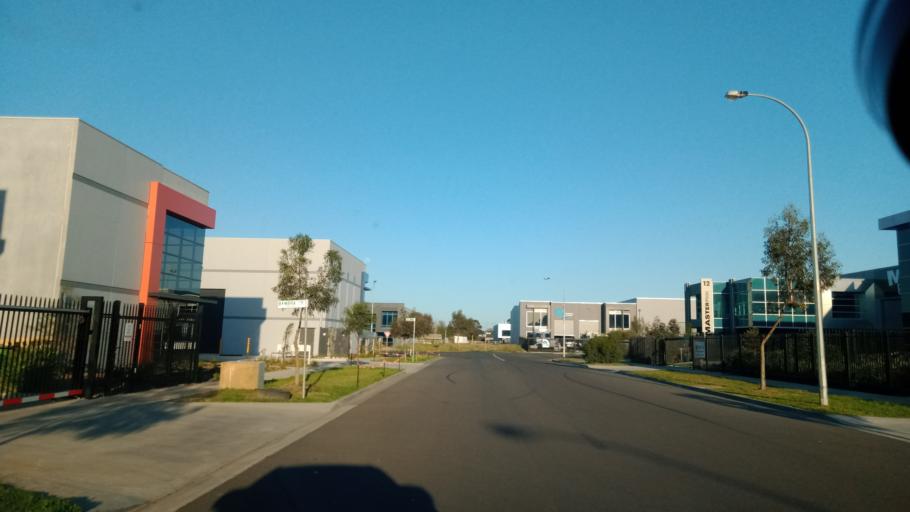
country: AU
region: Victoria
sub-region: Casey
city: Lynbrook
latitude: -38.0804
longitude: 145.2446
